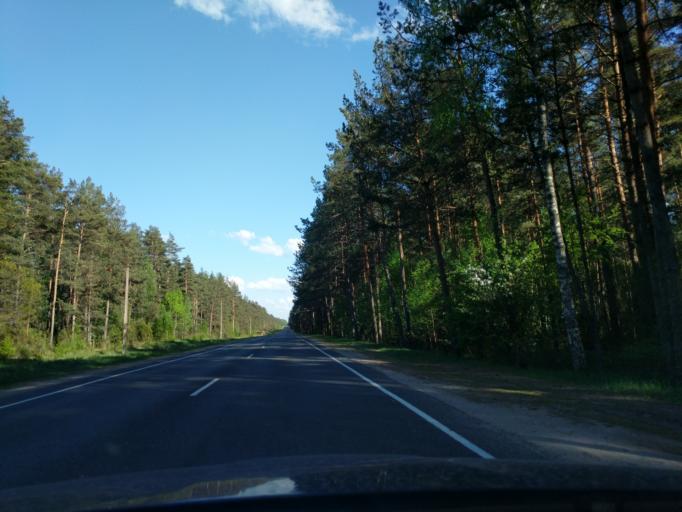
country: BY
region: Minsk
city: Myadzyel
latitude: 54.8255
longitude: 26.9474
